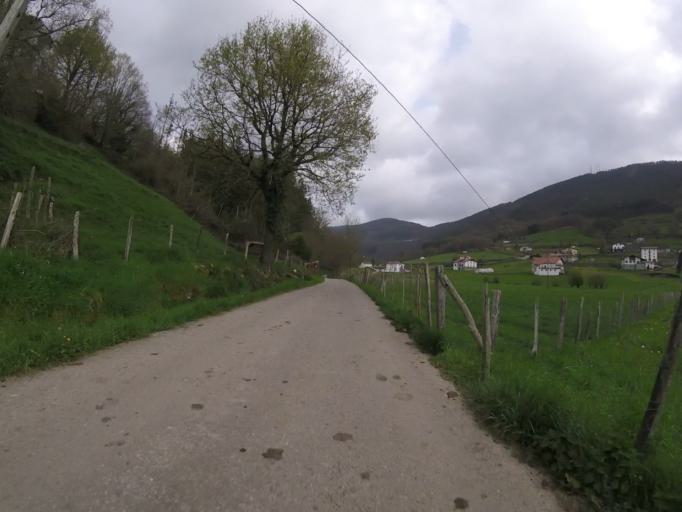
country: ES
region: Basque Country
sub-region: Provincia de Guipuzcoa
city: Berastegui
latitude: 43.1278
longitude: -1.9875
